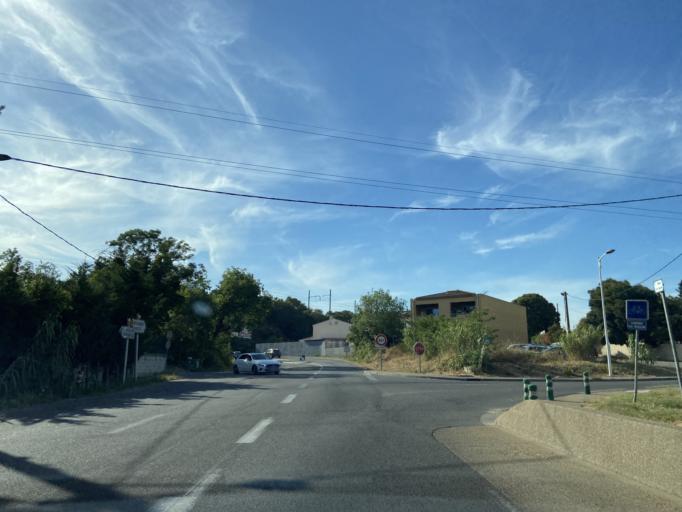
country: FR
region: Provence-Alpes-Cote d'Azur
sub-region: Departement des Bouches-du-Rhone
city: Miramas
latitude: 43.5762
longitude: 5.0149
